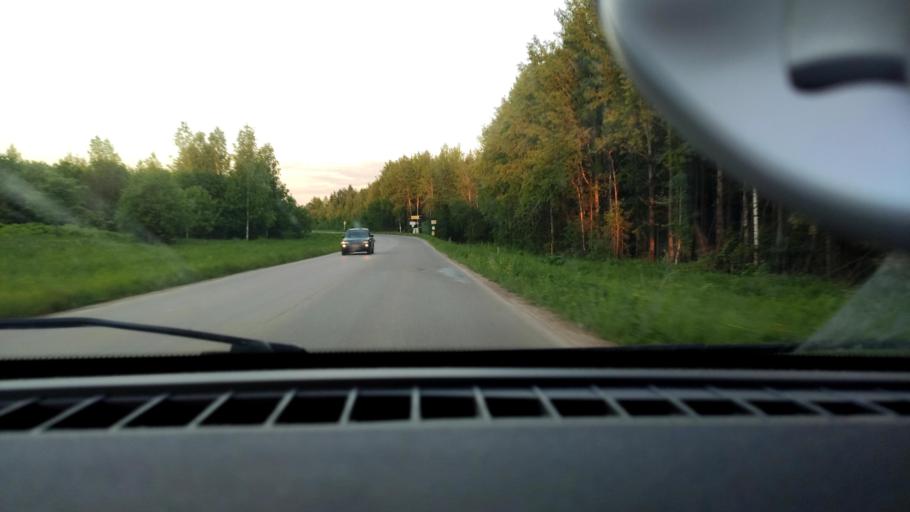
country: RU
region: Perm
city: Polazna
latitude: 58.2110
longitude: 56.4463
